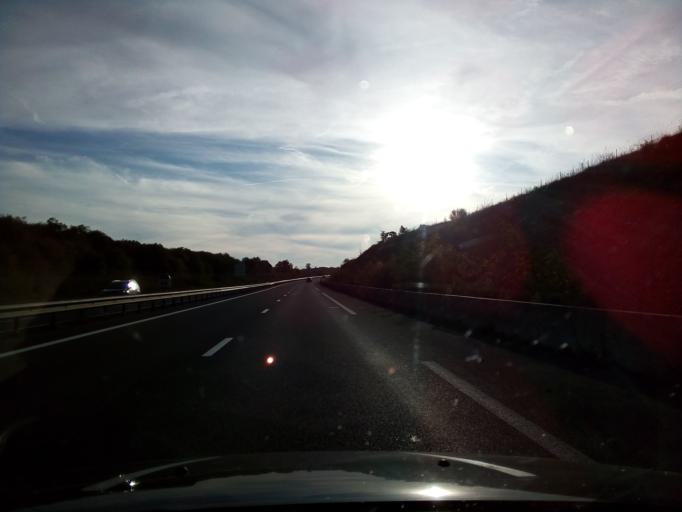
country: FR
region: Poitou-Charentes
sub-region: Departement de la Charente
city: Saint-Projet-Saint-Constant
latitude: 45.7334
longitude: 0.3376
